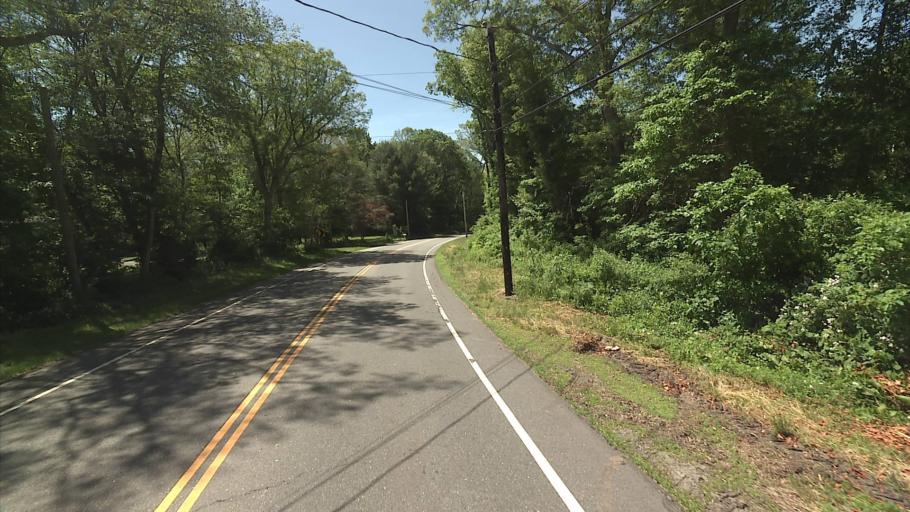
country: US
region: Rhode Island
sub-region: Washington County
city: Hopkinton
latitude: 41.4815
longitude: -71.8303
